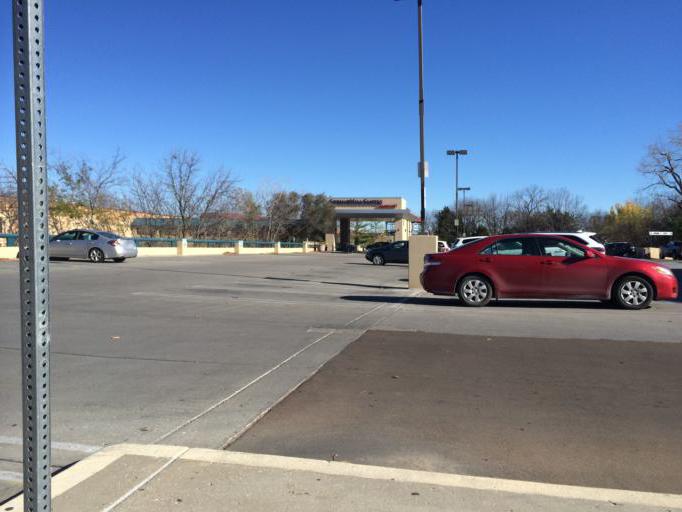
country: US
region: Kansas
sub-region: Douglas County
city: Lawrence
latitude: 38.9731
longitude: -95.2345
